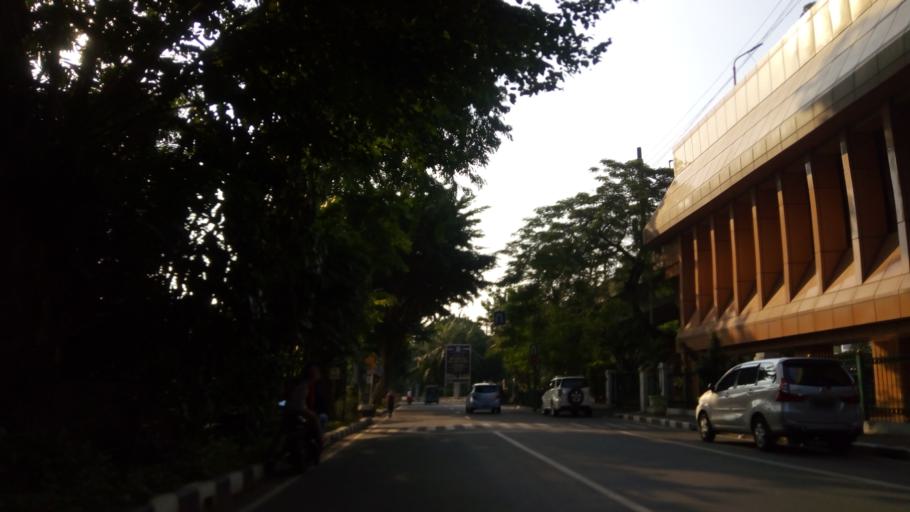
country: ID
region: Jakarta Raya
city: Jakarta
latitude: -6.1979
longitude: 106.8407
